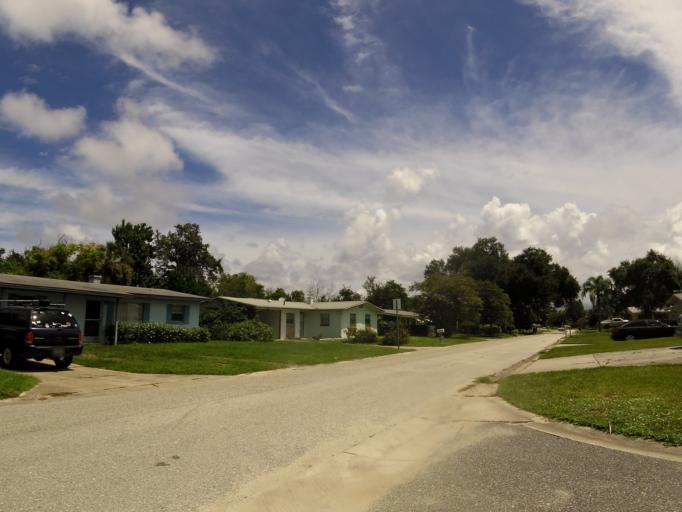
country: US
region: Florida
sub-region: Brevard County
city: Titusville
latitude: 28.6203
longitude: -80.8459
